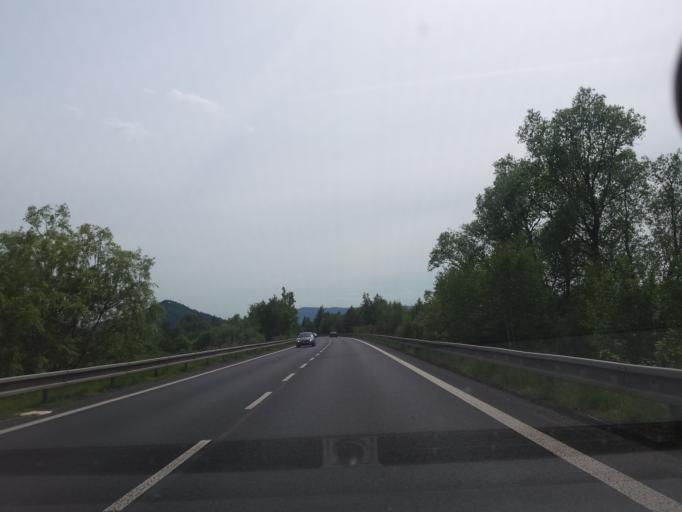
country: CZ
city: Novy Bor
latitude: 50.7628
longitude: 14.5379
